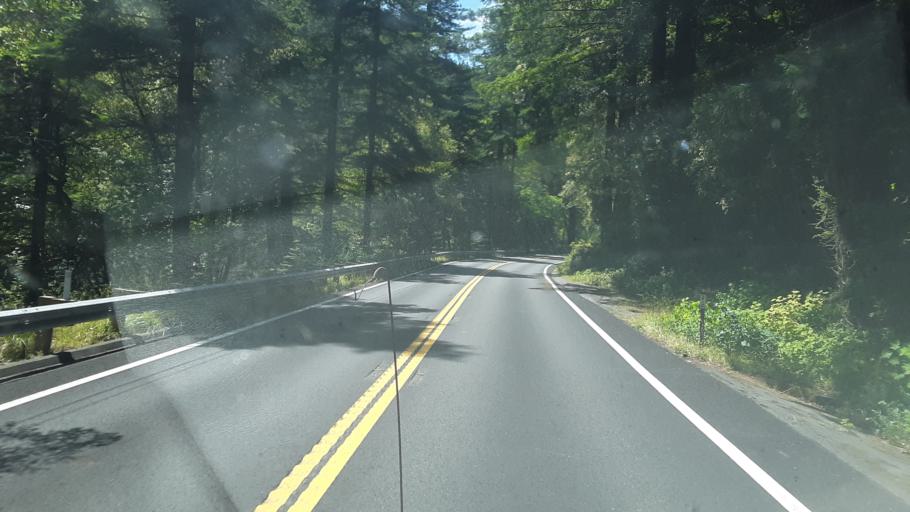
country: US
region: California
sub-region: Del Norte County
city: Bertsch-Oceanview
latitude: 41.8070
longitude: -124.0522
